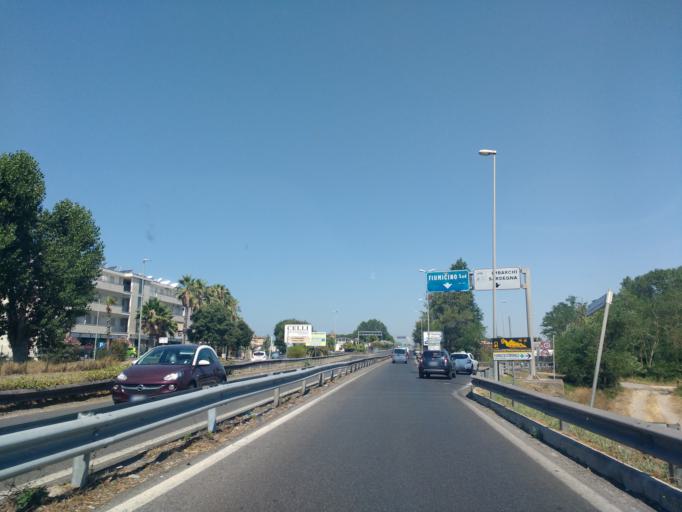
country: IT
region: Latium
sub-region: Citta metropolitana di Roma Capitale
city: Fiumicino-Isola Sacra
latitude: 41.7686
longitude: 12.2604
